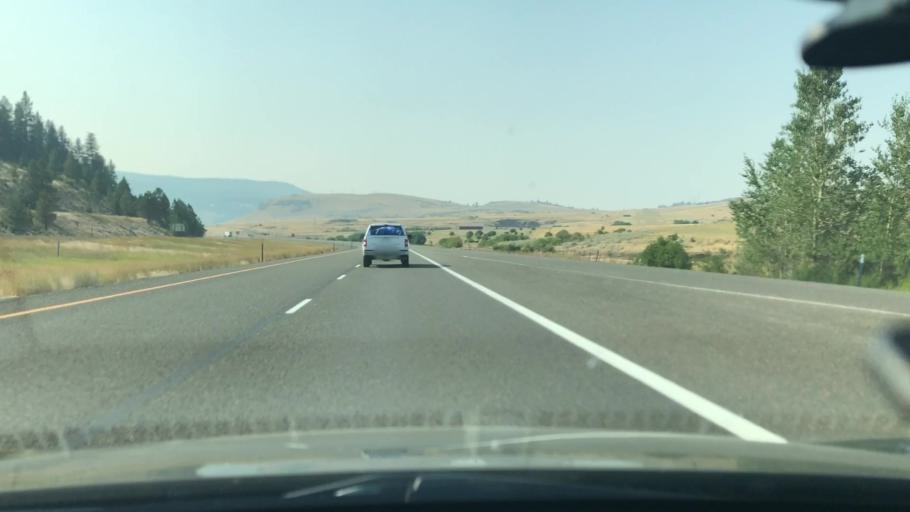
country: US
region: Oregon
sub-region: Union County
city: Union
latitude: 45.1846
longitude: -117.9885
